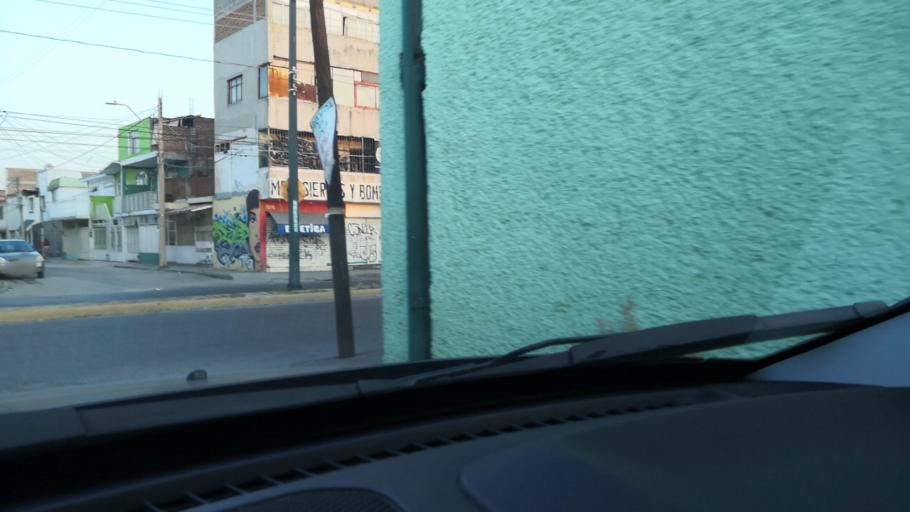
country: MX
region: Guanajuato
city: Leon
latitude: 21.1266
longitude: -101.6608
